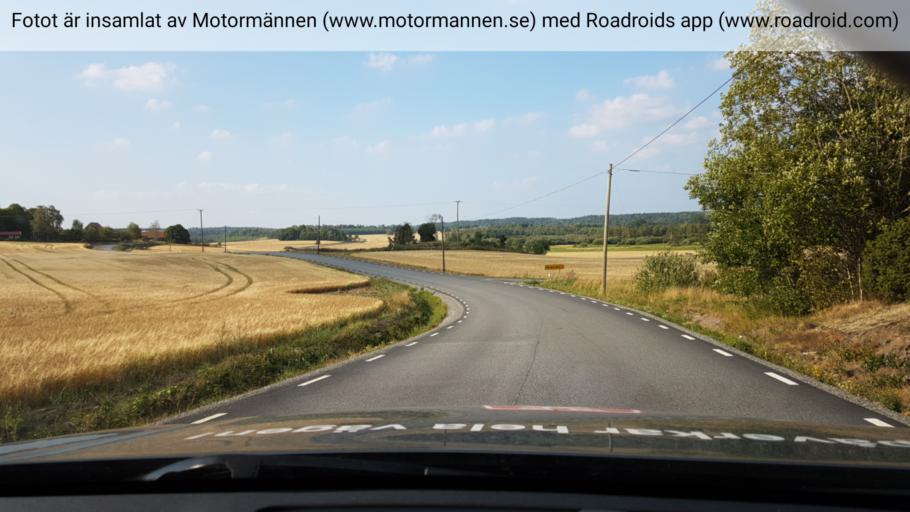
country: SE
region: Soedermanland
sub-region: Gnesta Kommun
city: Gnesta
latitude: 59.1235
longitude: 17.2159
